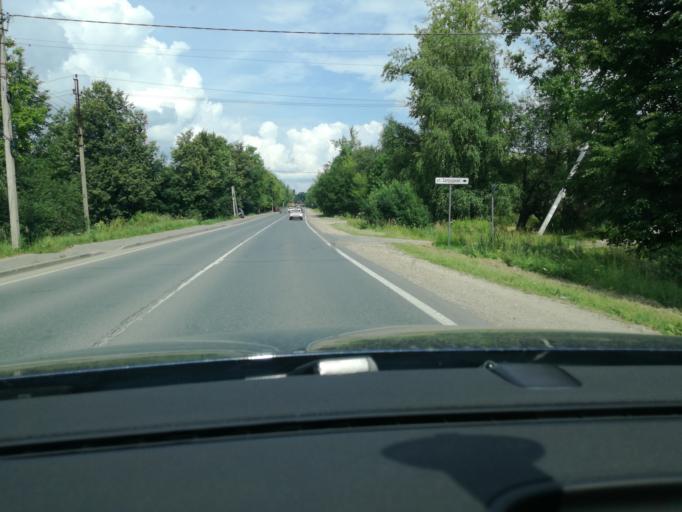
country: RU
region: Moskovskaya
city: Semkhoz
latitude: 56.2819
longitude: 38.0575
